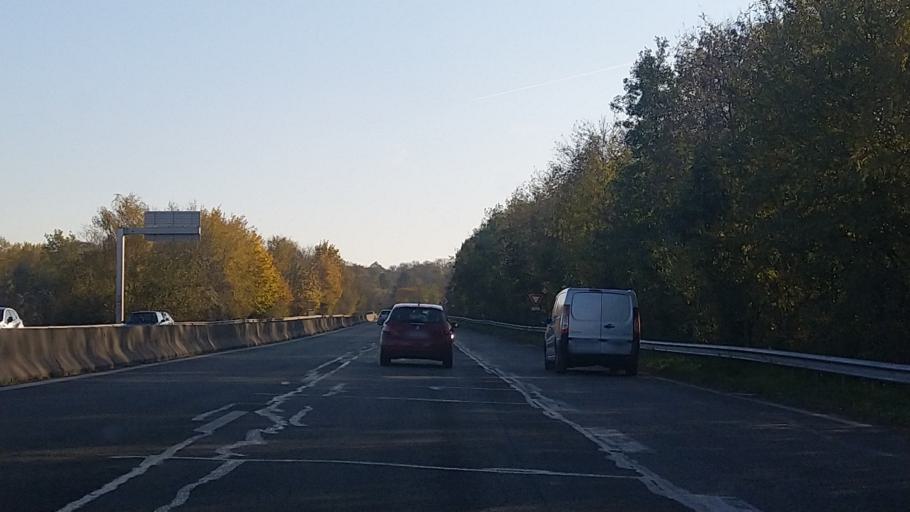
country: FR
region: Ile-de-France
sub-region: Departement du Val-d'Oise
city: Moisselles
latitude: 49.0331
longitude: 2.3462
